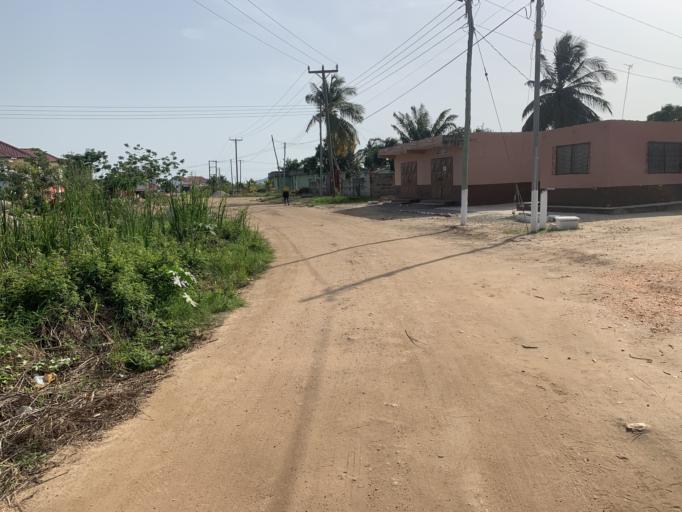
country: GH
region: Central
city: Winneba
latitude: 5.3649
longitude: -0.6410
